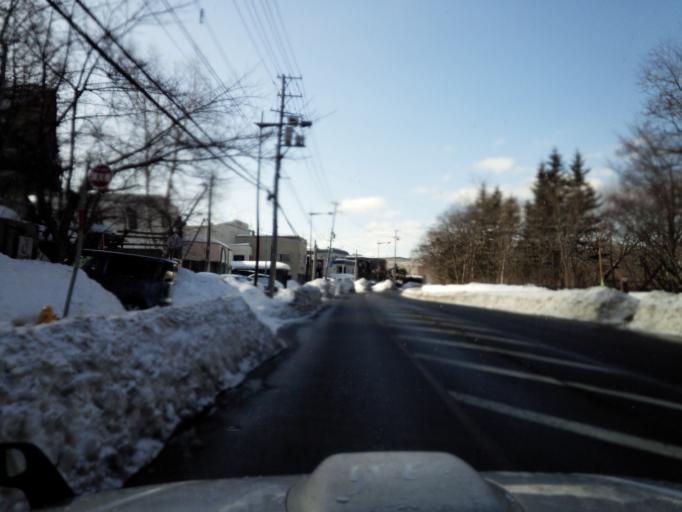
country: JP
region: Hokkaido
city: Sapporo
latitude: 42.9403
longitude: 141.3446
